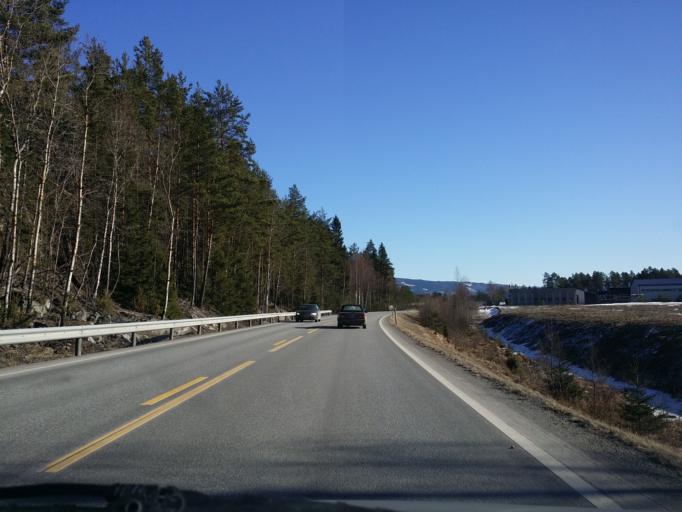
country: NO
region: Buskerud
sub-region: Ringerike
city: Honefoss
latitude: 60.2248
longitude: 10.2521
